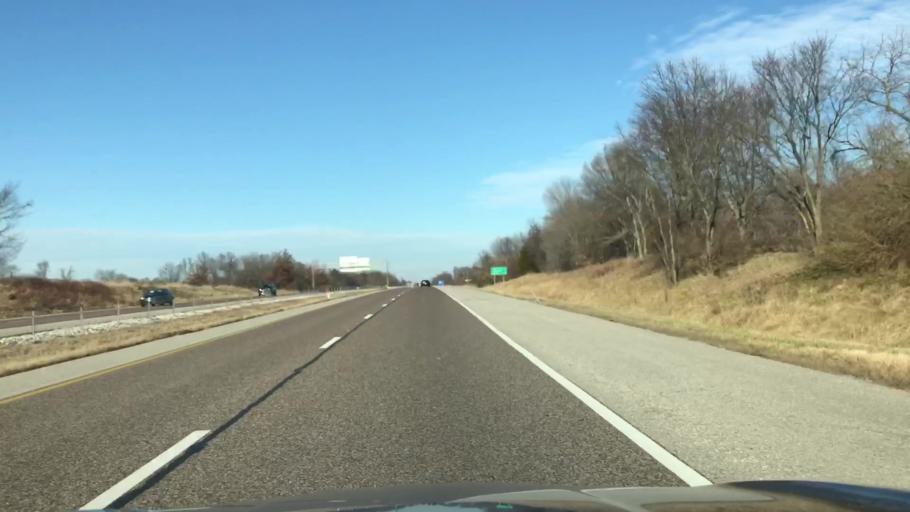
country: US
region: Illinois
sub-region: Madison County
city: Troy
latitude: 38.7668
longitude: -89.9030
